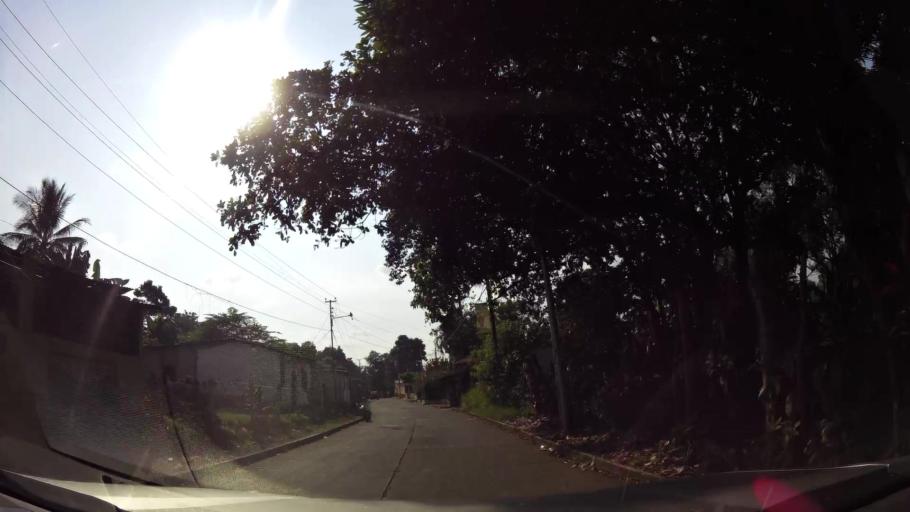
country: GT
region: Retalhuleu
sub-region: Municipio de Retalhuleu
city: Retalhuleu
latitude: 14.5369
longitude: -91.6918
